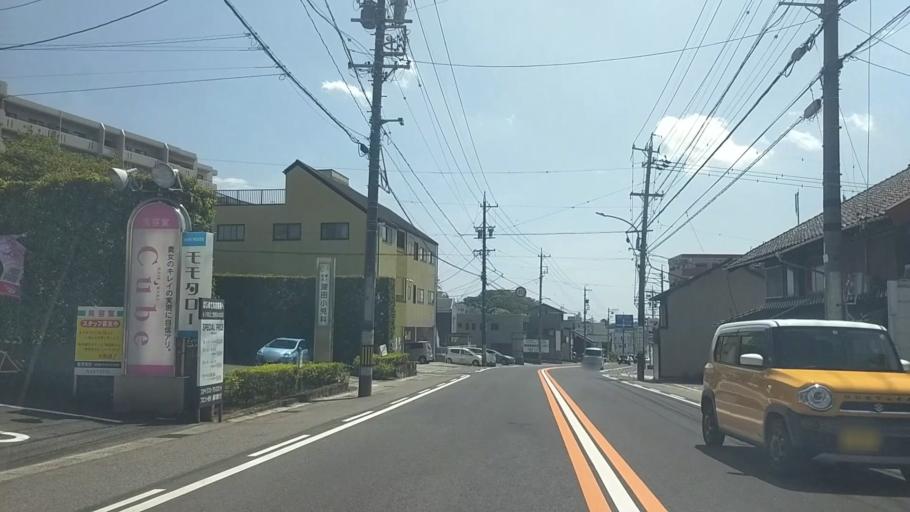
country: JP
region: Aichi
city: Okazaki
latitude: 34.9741
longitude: 137.1685
